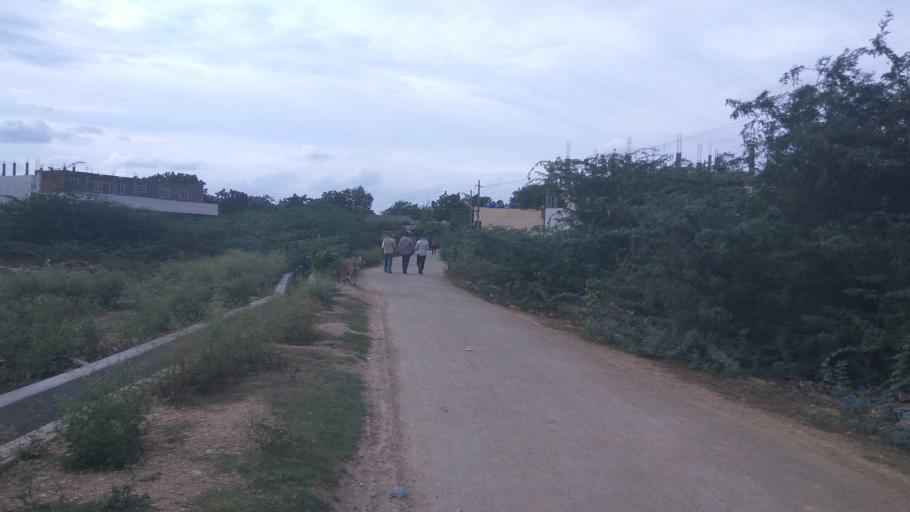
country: IN
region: Andhra Pradesh
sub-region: Prakasam
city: Cumbum
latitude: 15.5878
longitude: 79.1114
